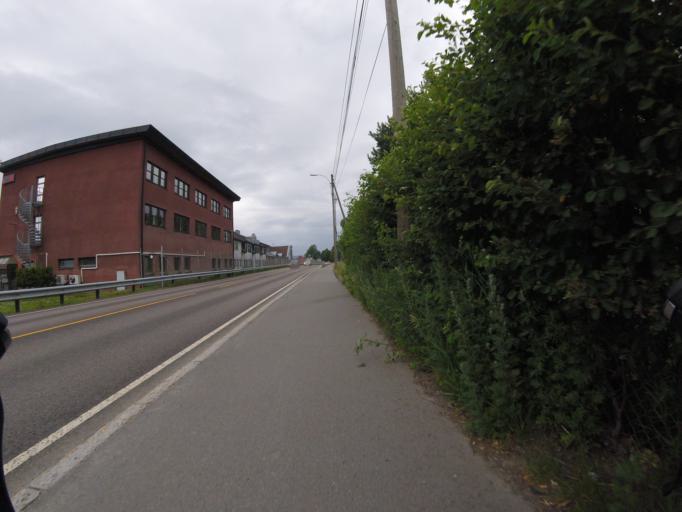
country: NO
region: Akershus
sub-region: Skedsmo
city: Lillestrom
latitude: 59.9733
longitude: 11.0397
